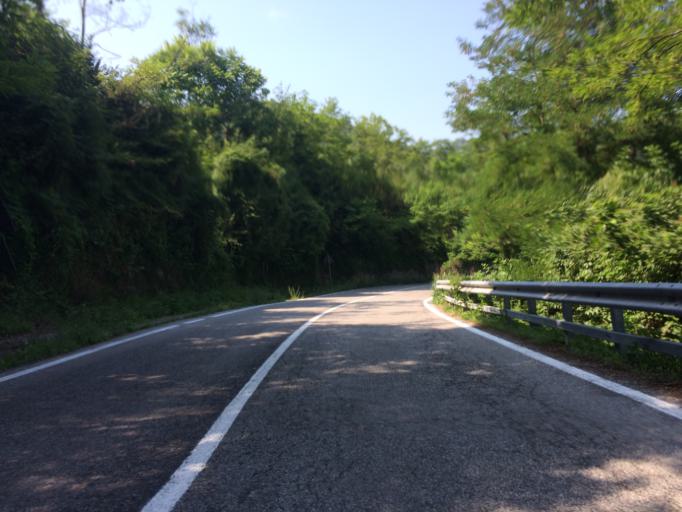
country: IT
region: Piedmont
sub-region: Provincia di Cuneo
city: Torre Bormida
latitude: 44.5764
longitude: 8.1655
